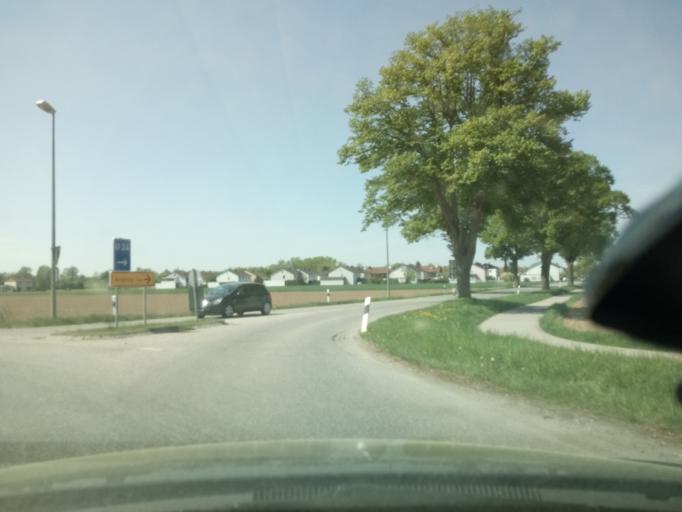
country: DE
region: Bavaria
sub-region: Upper Bavaria
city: Neufahrn
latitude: 48.2565
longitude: 12.4328
